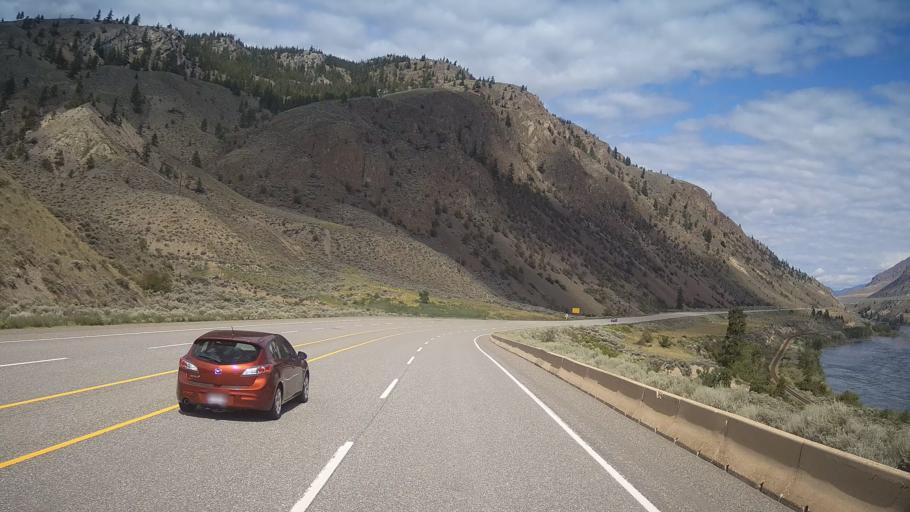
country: CA
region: British Columbia
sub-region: Thompson-Nicola Regional District
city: Ashcroft
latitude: 50.5178
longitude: -121.2830
